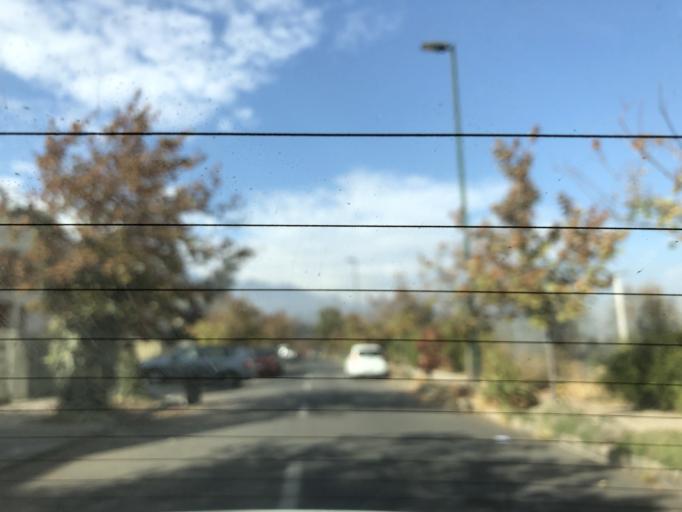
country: CL
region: Santiago Metropolitan
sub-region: Provincia de Cordillera
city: Puente Alto
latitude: -33.5935
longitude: -70.5348
